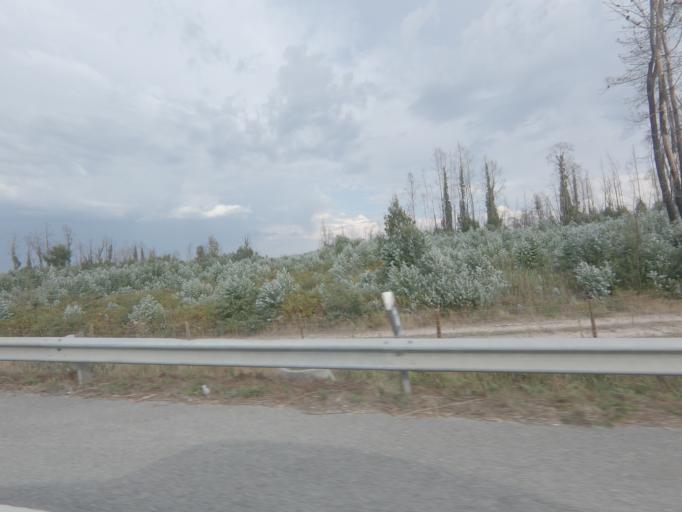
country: PT
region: Viseu
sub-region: Santa Comba Dao
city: Santa Comba Dao
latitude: 40.4535
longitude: -8.1046
